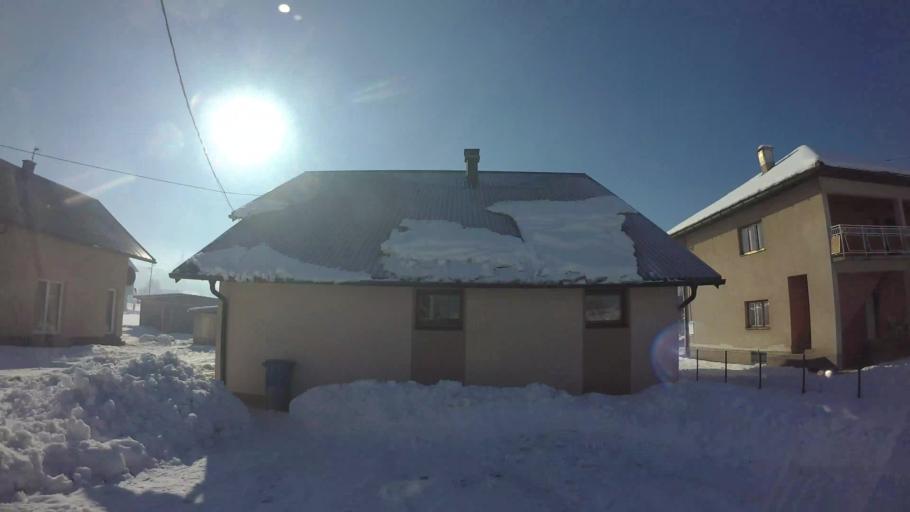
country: BA
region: Federation of Bosnia and Herzegovina
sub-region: Kanton Sarajevo
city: Sarajevo
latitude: 43.7938
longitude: 18.3470
